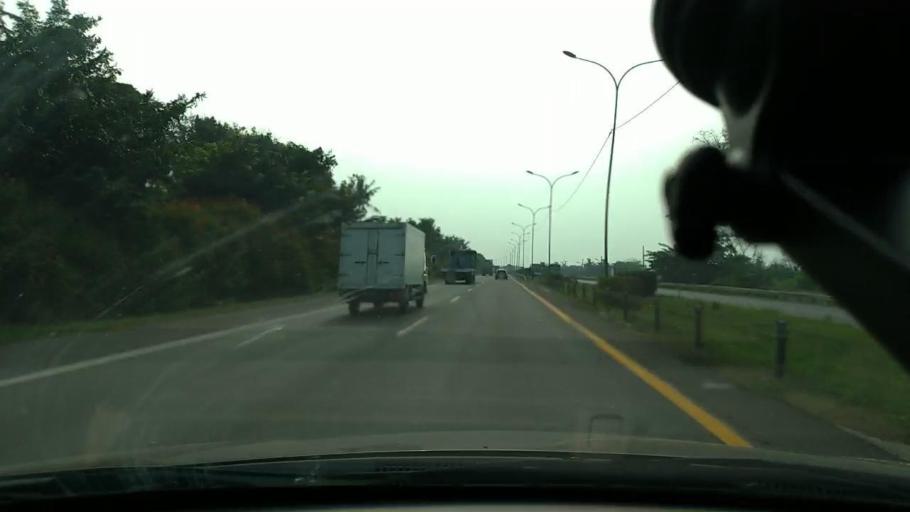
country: ID
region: Banten
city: Serang
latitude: -6.1046
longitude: 106.1758
